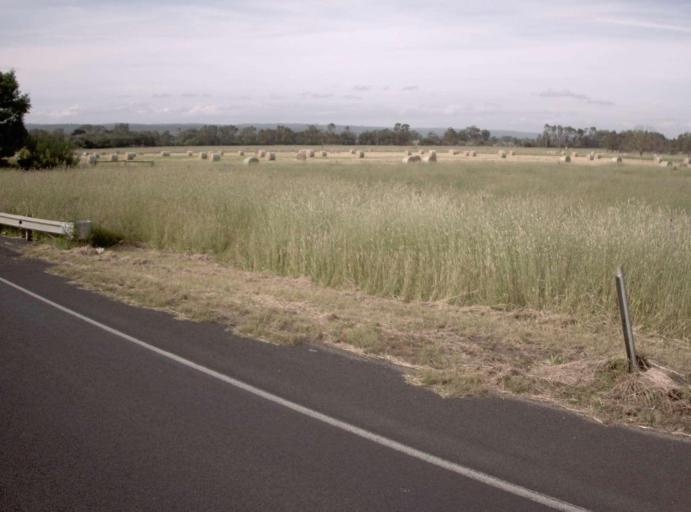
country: AU
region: Victoria
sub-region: Latrobe
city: Traralgon
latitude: -38.1604
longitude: 146.5550
